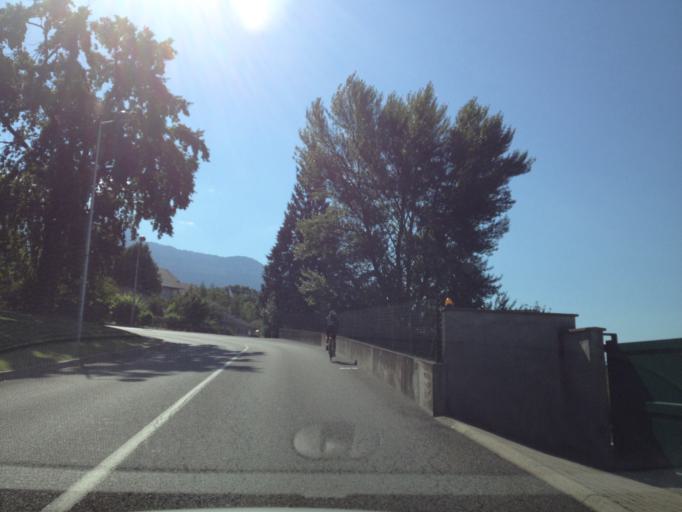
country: FR
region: Rhone-Alpes
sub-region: Departement de la Savoie
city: Gresy-sur-Aix
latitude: 45.7208
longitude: 5.9270
